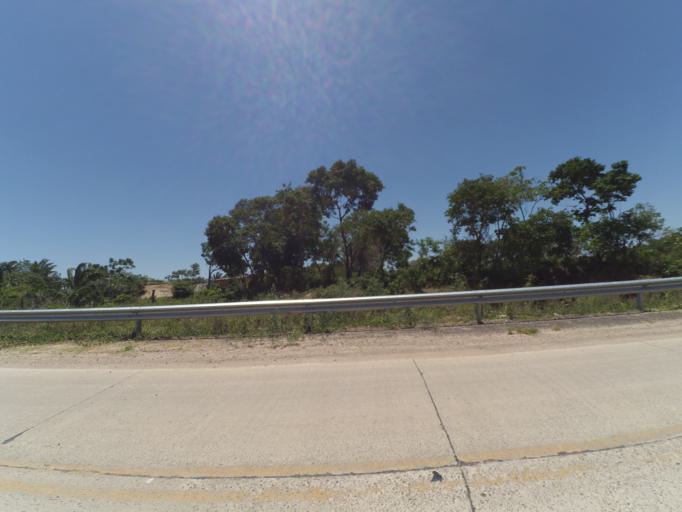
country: BO
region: Santa Cruz
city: Santa Cruz de la Sierra
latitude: -17.8283
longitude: -63.2909
